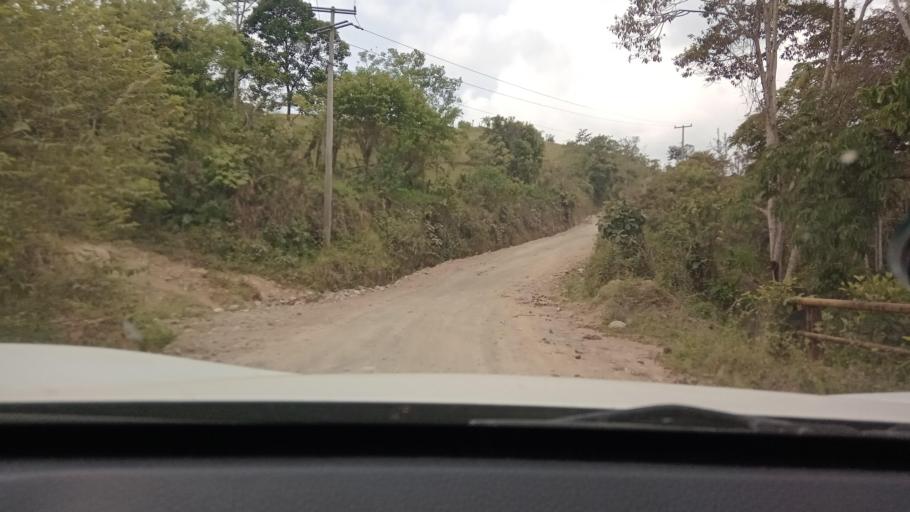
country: MX
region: Tabasco
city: Chontalpa
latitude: 17.5008
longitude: -93.6443
